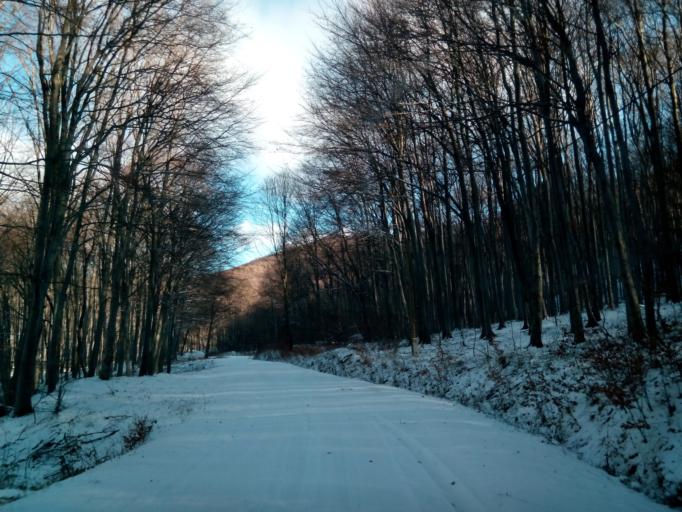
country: HU
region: Borsod-Abauj-Zemplen
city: Gonc
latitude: 48.5700
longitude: 21.4375
